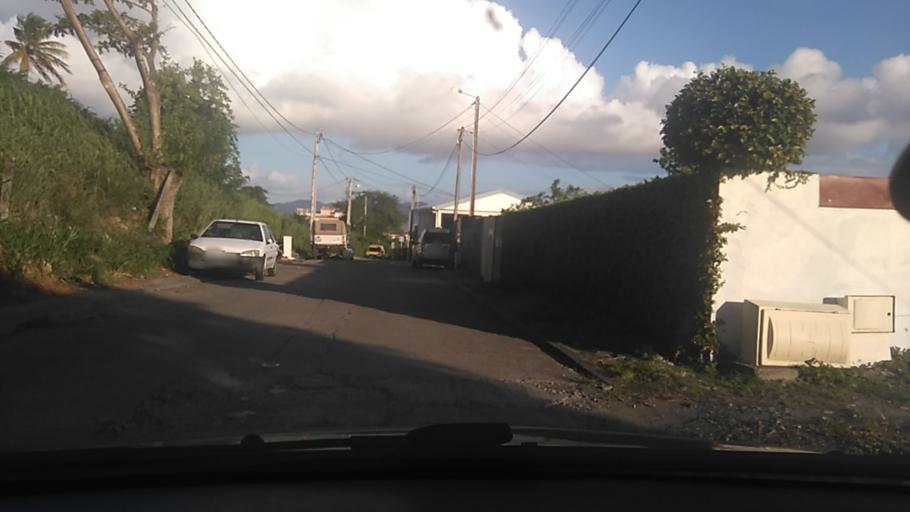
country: MQ
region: Martinique
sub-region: Martinique
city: Fort-de-France
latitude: 14.6024
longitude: -61.0923
